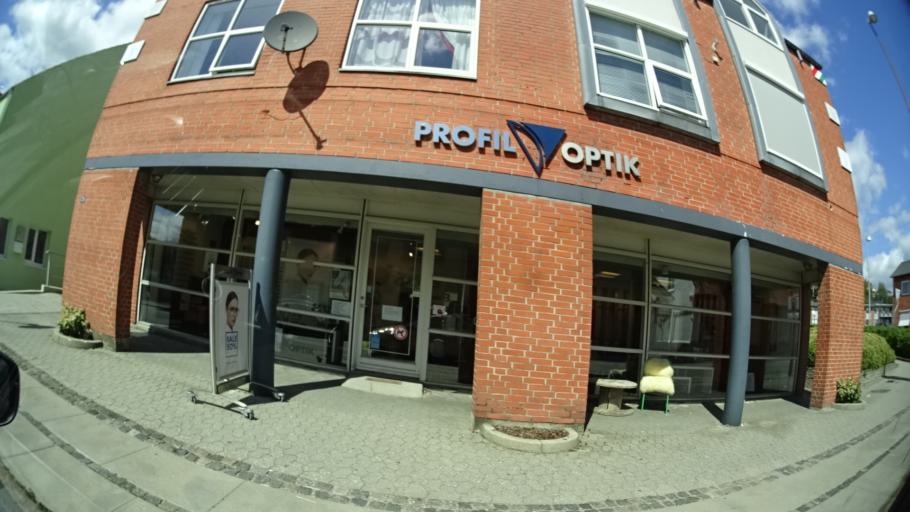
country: DK
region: Central Jutland
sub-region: Syddjurs Kommune
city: Ronde
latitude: 56.3003
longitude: 10.4771
